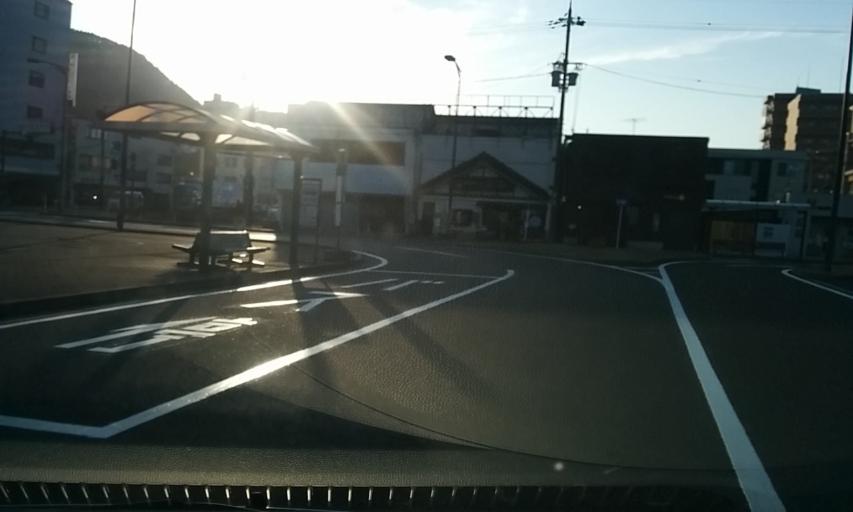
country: JP
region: Kyoto
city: Ayabe
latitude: 35.3017
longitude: 135.2527
